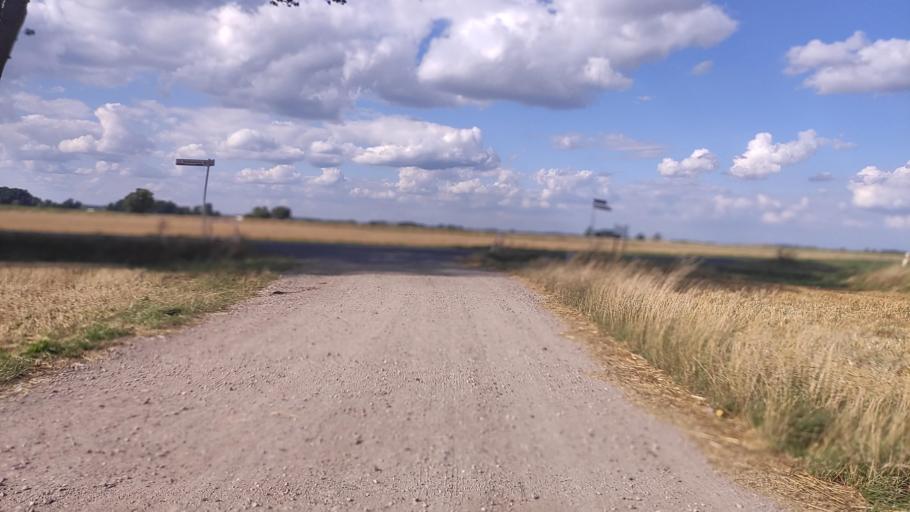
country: PL
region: Greater Poland Voivodeship
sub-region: Powiat poznanski
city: Swarzedz
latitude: 52.4197
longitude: 17.1419
